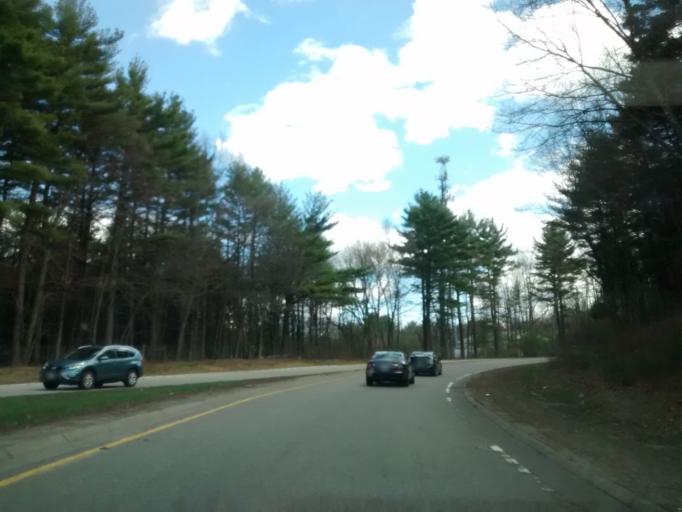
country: US
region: Massachusetts
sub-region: Middlesex County
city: Hopkinton
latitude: 42.2146
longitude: -71.5439
